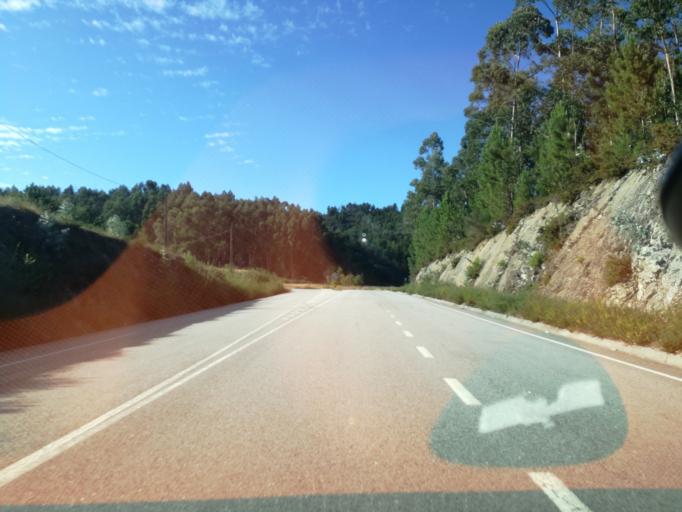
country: PT
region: Porto
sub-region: Pacos de Ferreira
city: Seroa
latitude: 41.2823
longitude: -8.4242
